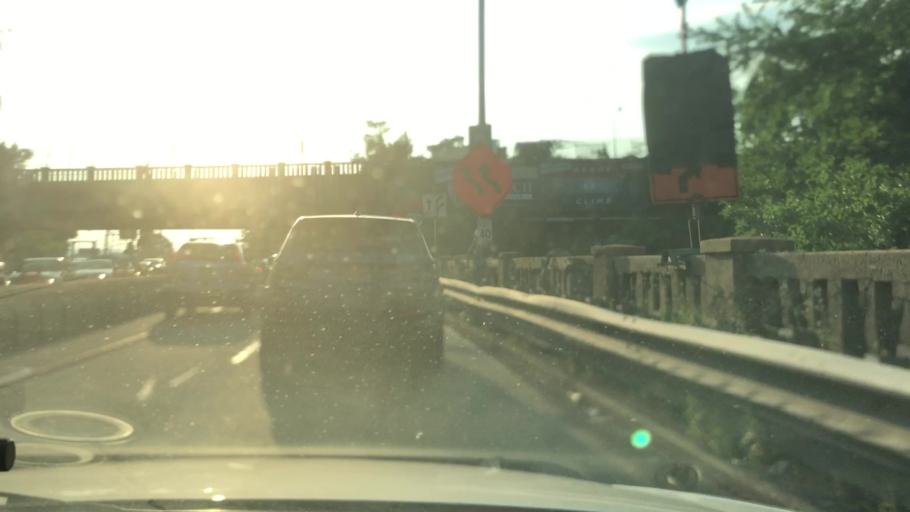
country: US
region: New Jersey
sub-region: Hudson County
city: Jersey City
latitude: 40.7388
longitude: -74.0613
